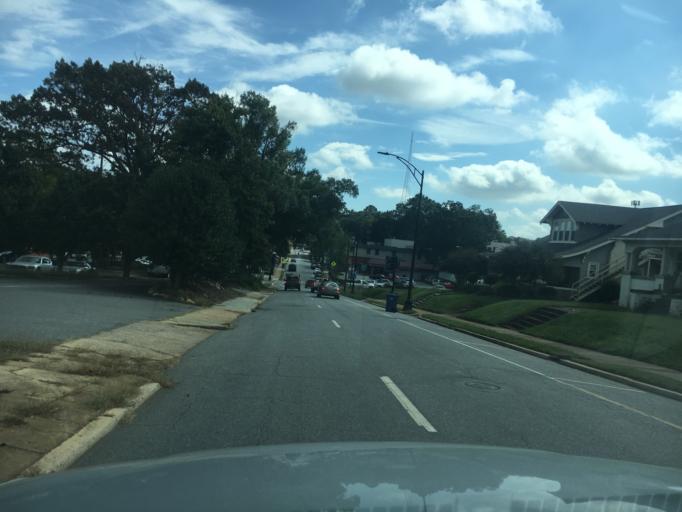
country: US
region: North Carolina
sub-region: Catawba County
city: Hickory
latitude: 35.7344
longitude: -81.3393
